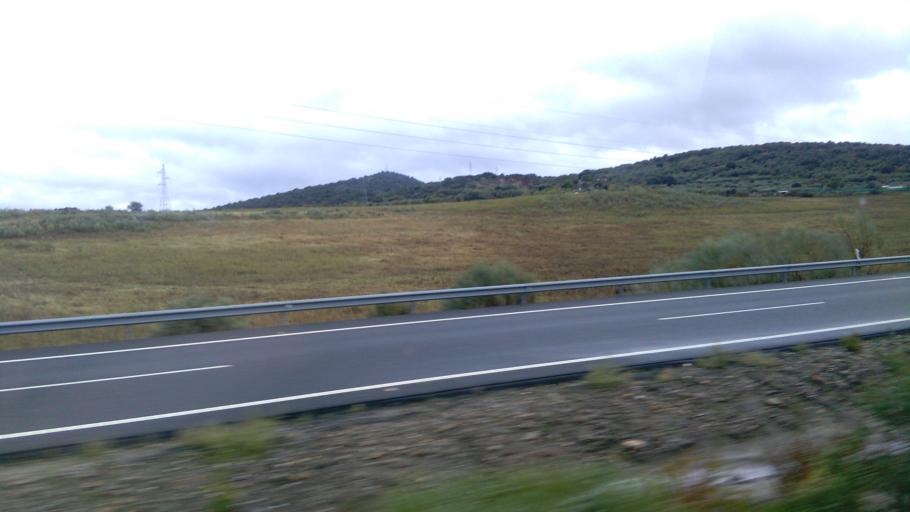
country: ES
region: Extremadura
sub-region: Provincia de Caceres
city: Almaraz
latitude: 39.8158
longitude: -5.6647
